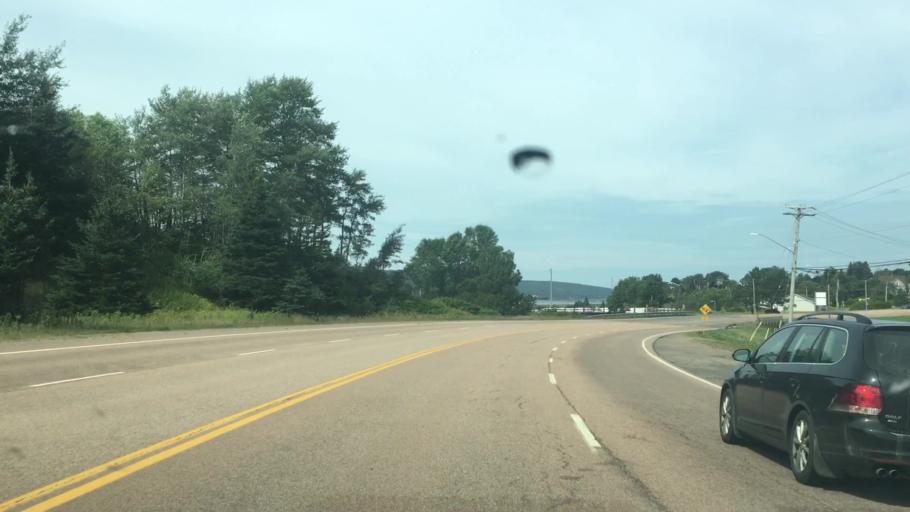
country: CA
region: Nova Scotia
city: Port Hawkesbury
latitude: 45.6213
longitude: -61.3628
